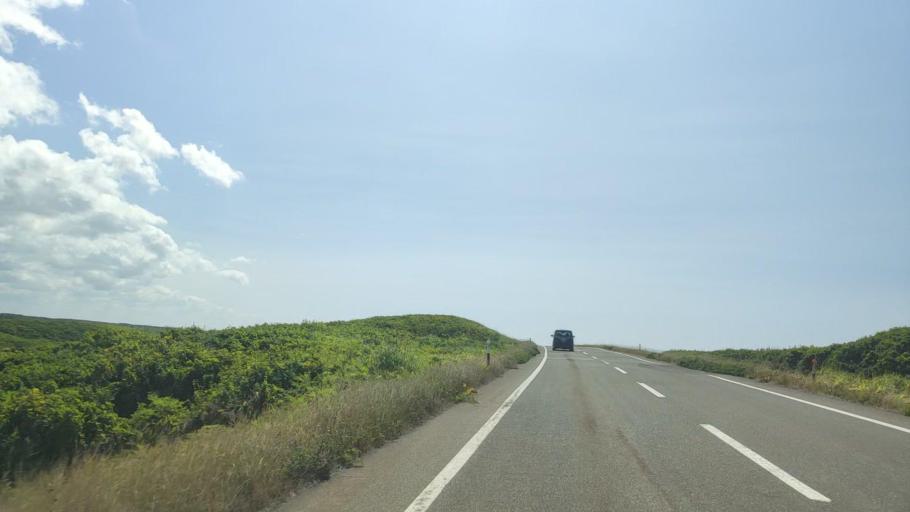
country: JP
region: Hokkaido
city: Wakkanai
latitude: 45.2079
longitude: 141.5710
